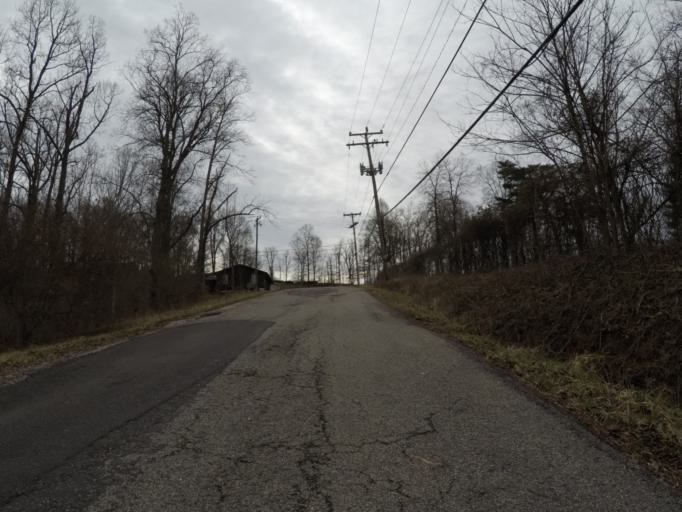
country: US
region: Ohio
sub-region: Lawrence County
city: Burlington
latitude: 38.3817
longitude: -82.5167
